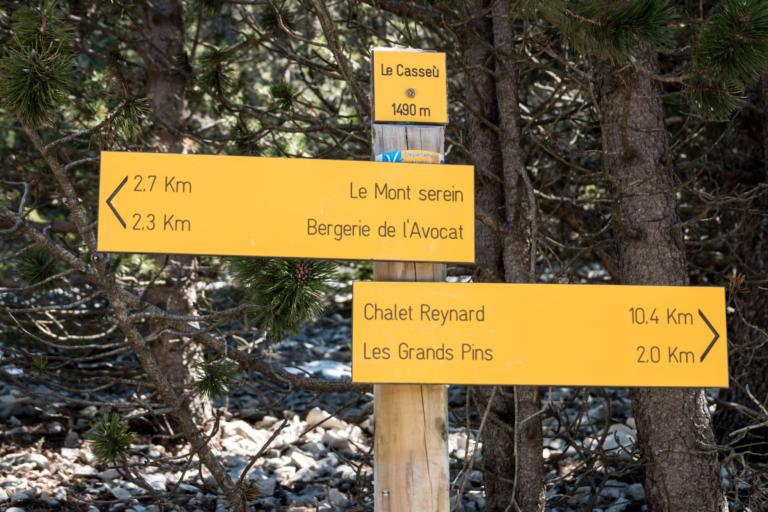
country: FR
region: Provence-Alpes-Cote d'Azur
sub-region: Departement du Vaucluse
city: Bedoin
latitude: 44.1719
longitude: 5.2372
